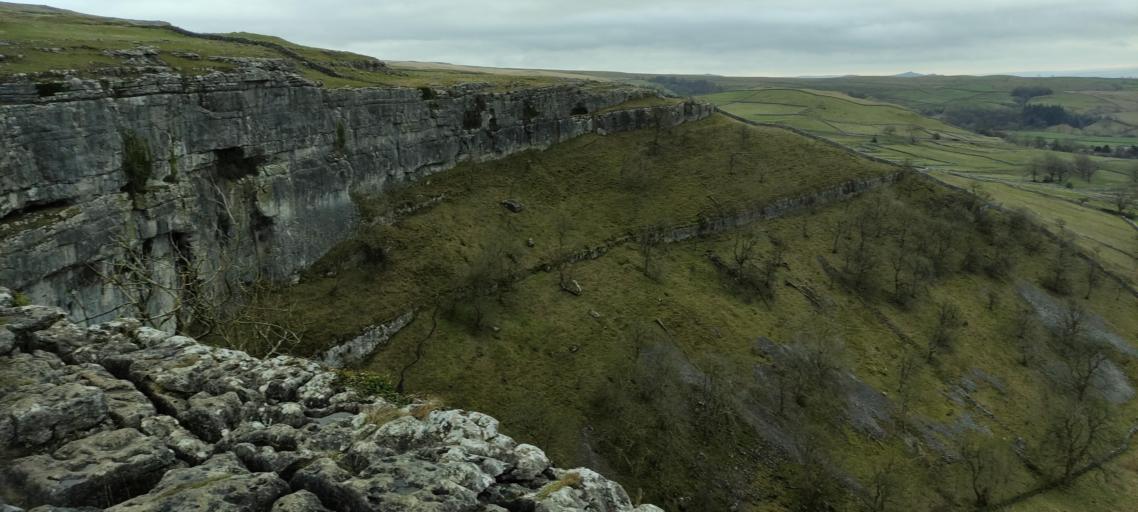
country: GB
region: England
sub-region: North Yorkshire
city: Gargrave
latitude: 54.0731
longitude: -2.1593
